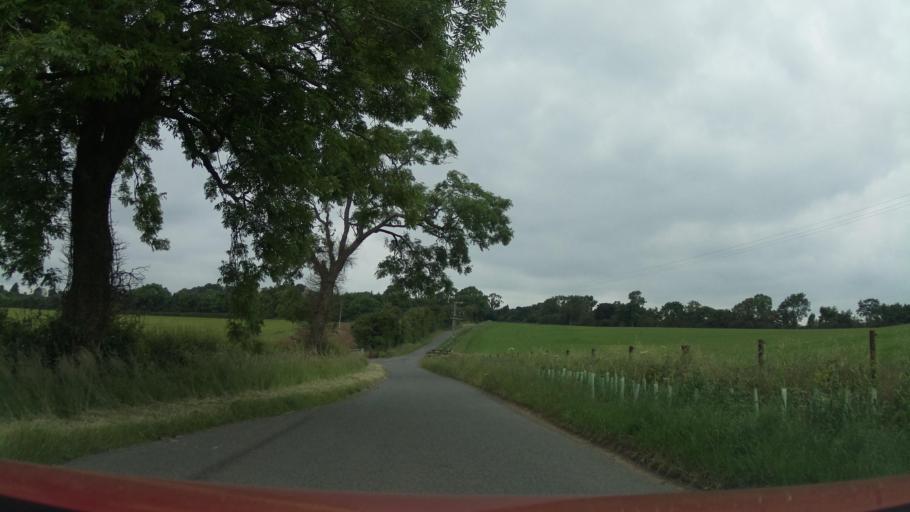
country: GB
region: England
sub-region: District of Rutland
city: Langham
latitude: 52.6783
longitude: -0.7950
